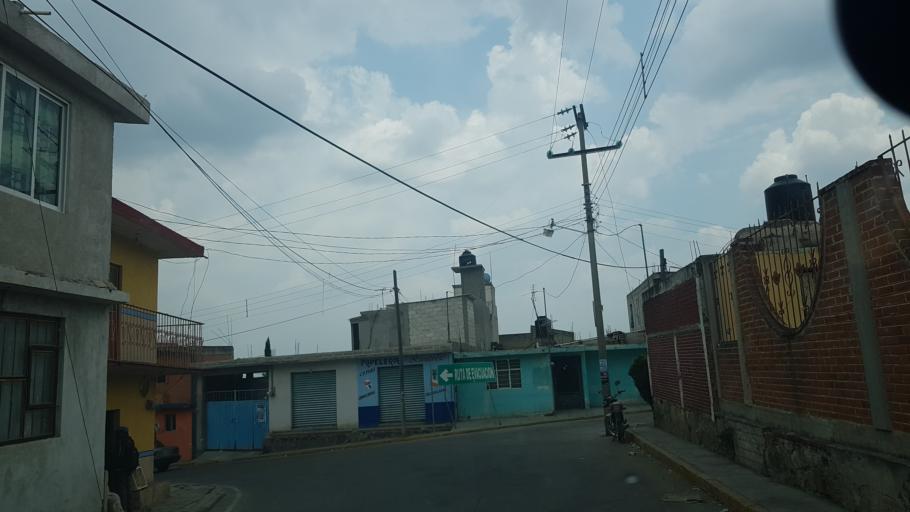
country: MX
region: Puebla
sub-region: Huejotzingo
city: San Miguel Tianguizolco
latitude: 19.1592
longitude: -98.4413
